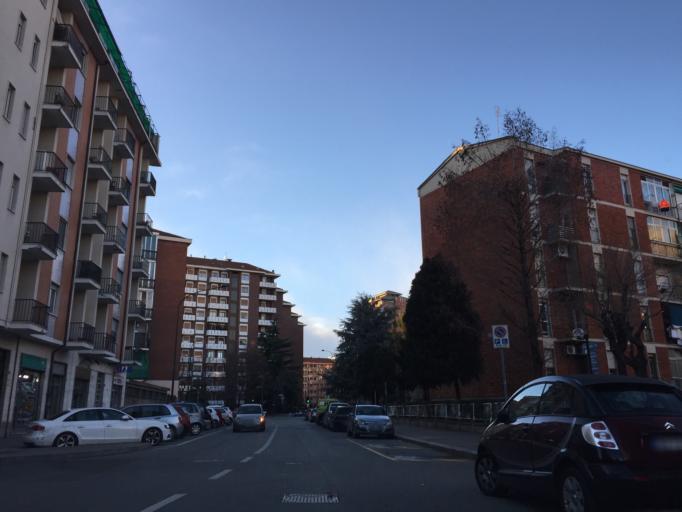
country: IT
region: Piedmont
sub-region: Provincia di Torino
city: Lesna
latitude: 45.0443
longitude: 7.6304
